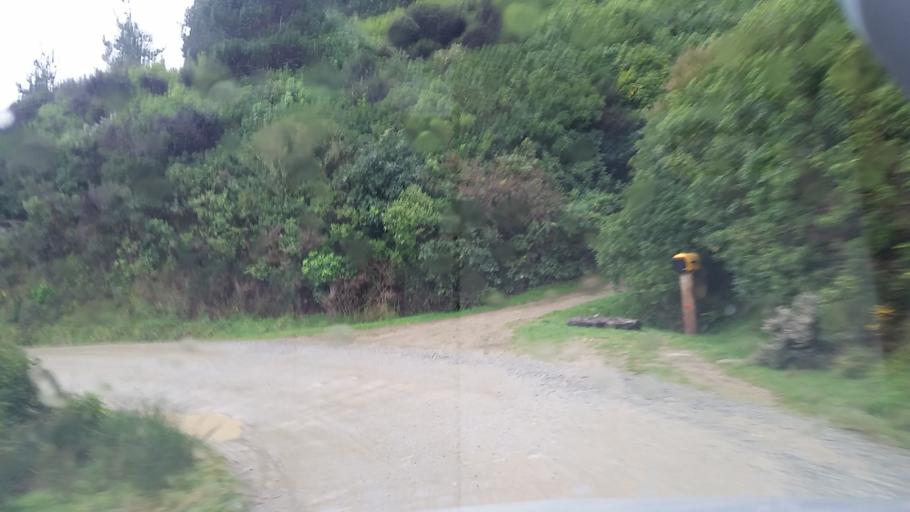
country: NZ
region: Marlborough
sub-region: Marlborough District
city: Picton
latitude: -41.1750
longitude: 174.0406
